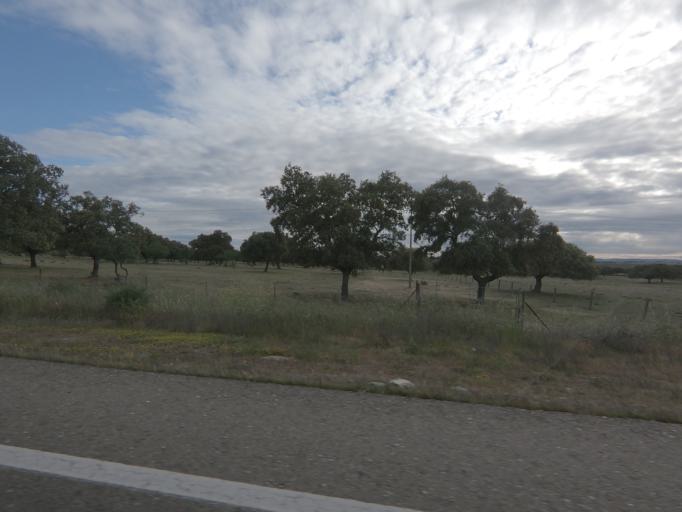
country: ES
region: Extremadura
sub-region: Provincia de Caceres
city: Torrejoncillo
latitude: 39.9213
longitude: -6.4941
